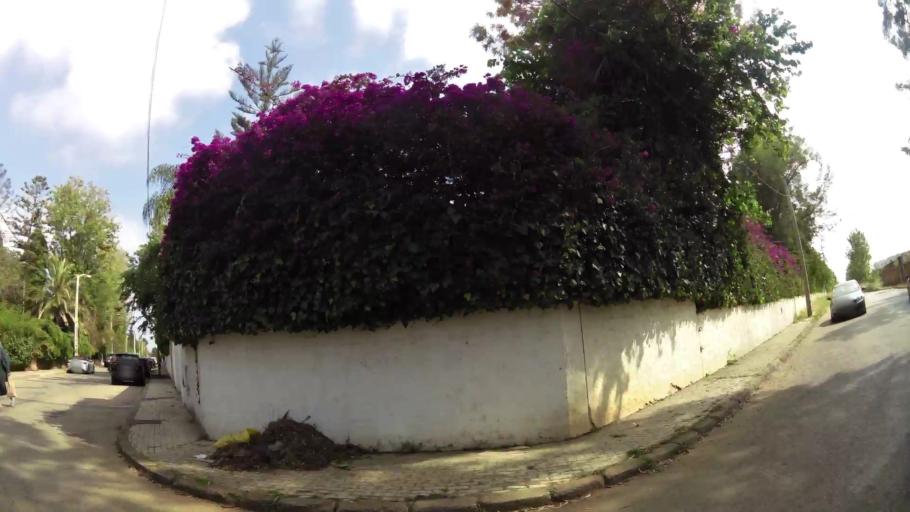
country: MA
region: Rabat-Sale-Zemmour-Zaer
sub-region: Rabat
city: Rabat
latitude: 33.9740
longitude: -6.8477
